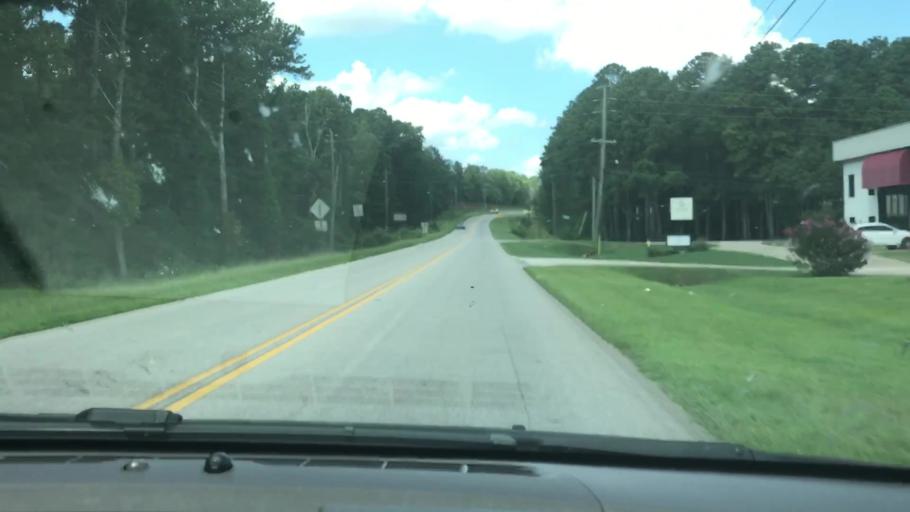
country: US
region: Georgia
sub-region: Troup County
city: La Grange
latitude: 33.0184
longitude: -85.0743
